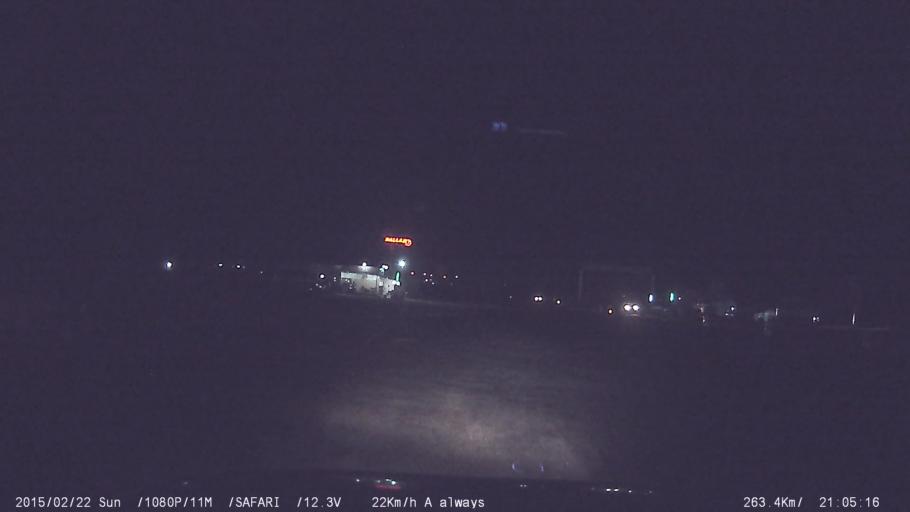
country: IN
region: Tamil Nadu
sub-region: Karur
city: Pallappatti
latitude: 10.6999
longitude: 77.9330
